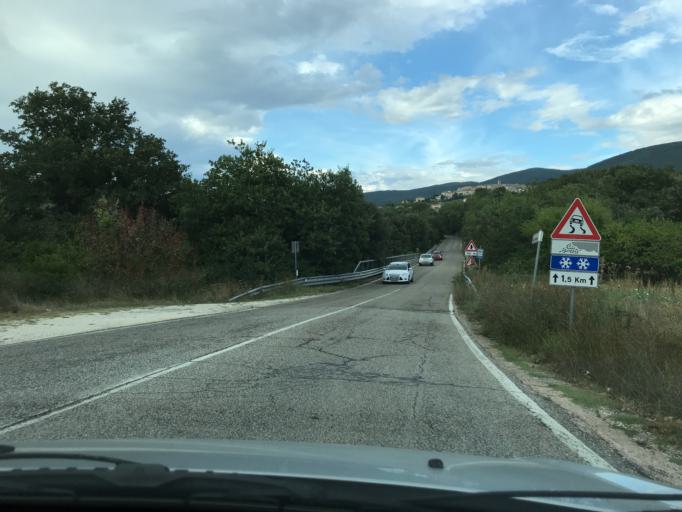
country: IT
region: Umbria
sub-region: Provincia di Terni
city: Montecchio
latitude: 42.6524
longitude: 12.2793
